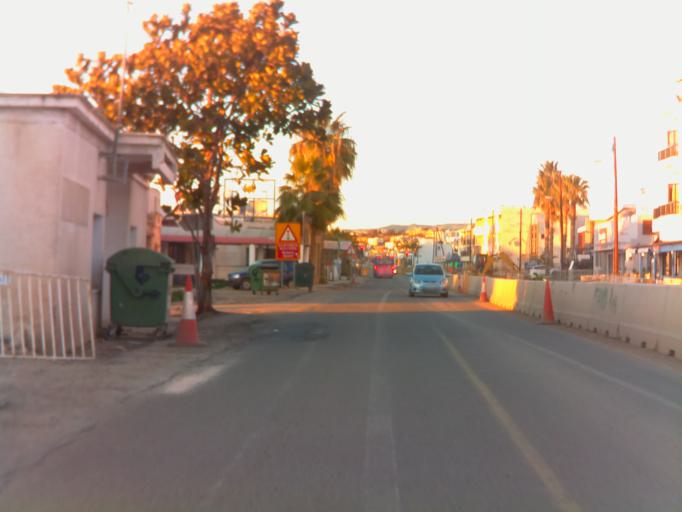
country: CY
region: Pafos
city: Paphos
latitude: 34.7673
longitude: 32.4105
